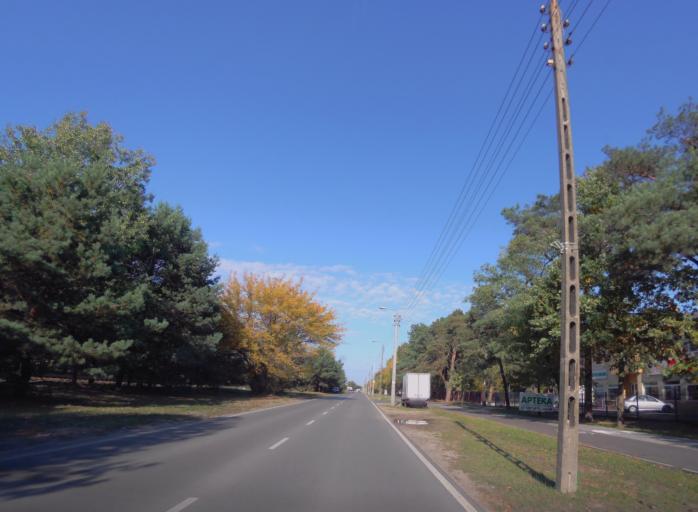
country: PL
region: Masovian Voivodeship
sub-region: Powiat otwocki
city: Jozefow
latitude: 52.1516
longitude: 21.2218
